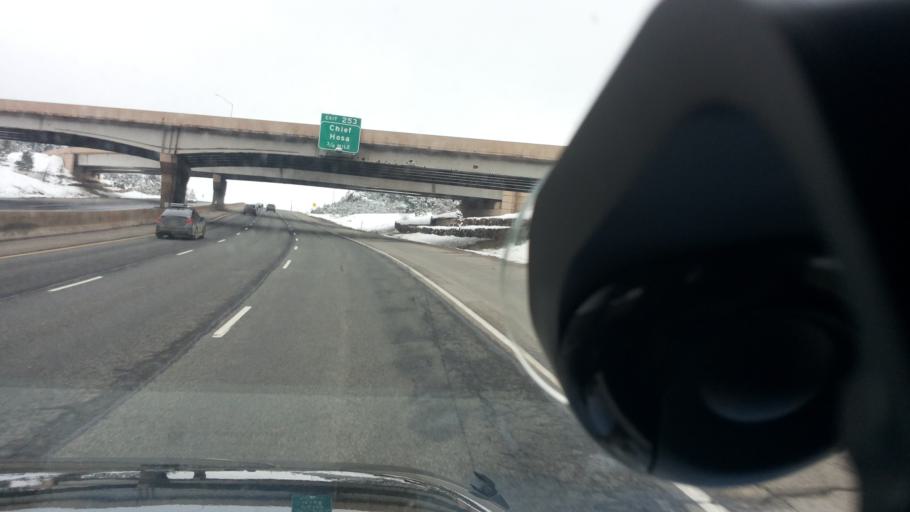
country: US
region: Colorado
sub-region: Jefferson County
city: Kittredge
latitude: 39.7019
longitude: -105.3302
